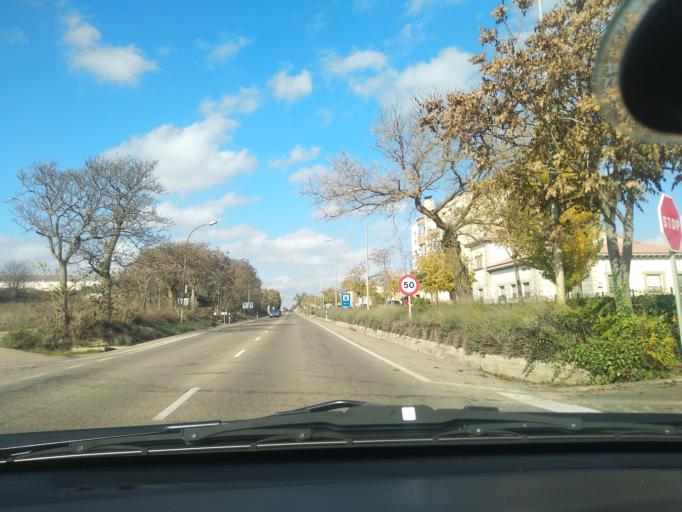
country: ES
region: Castille and Leon
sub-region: Provincia de Valladolid
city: Medina de Rioseco
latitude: 41.8865
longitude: -5.0489
